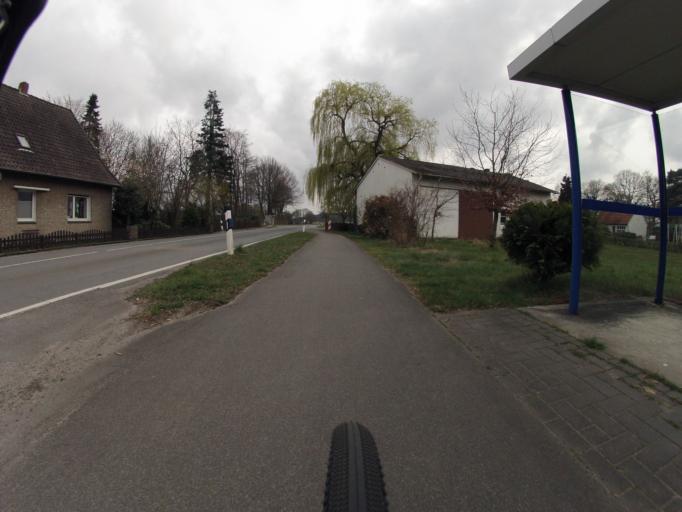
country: DE
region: North Rhine-Westphalia
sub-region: Regierungsbezirk Munster
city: Recke
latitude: 52.3472
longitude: 7.7136
